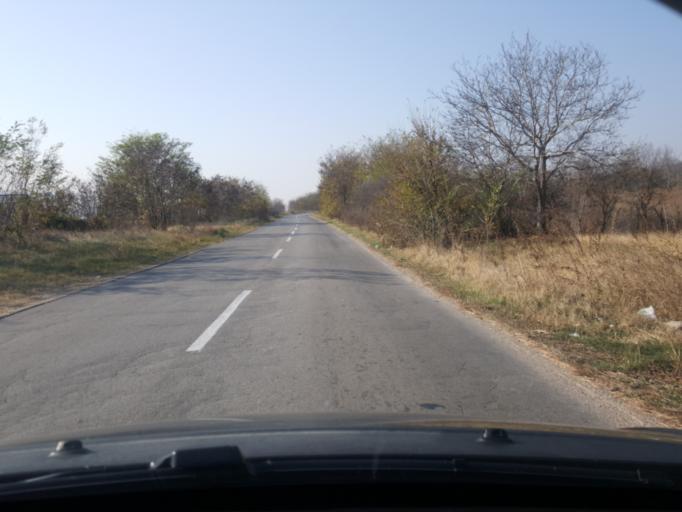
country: RS
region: Central Serbia
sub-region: Nisavski Okrug
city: Niska Banja
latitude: 43.3189
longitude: 22.0083
